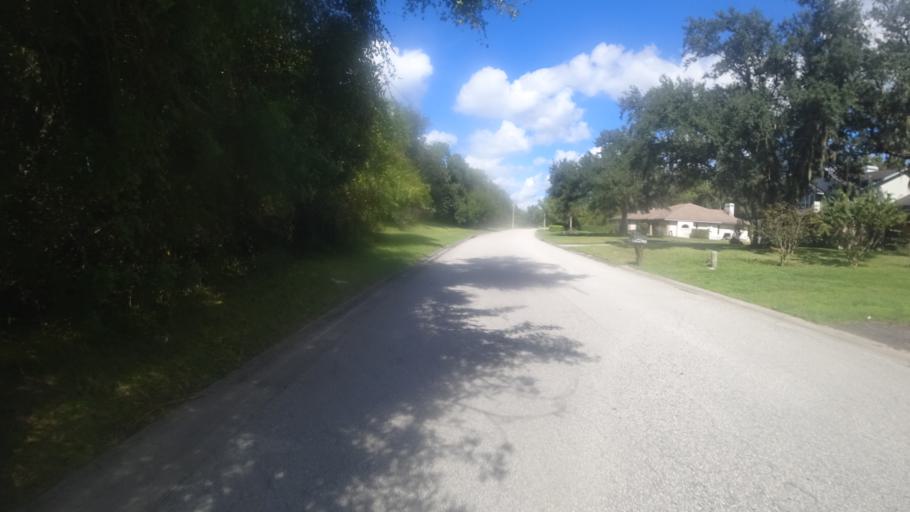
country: US
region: Florida
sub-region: Manatee County
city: Ellenton
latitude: 27.4880
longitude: -82.4090
